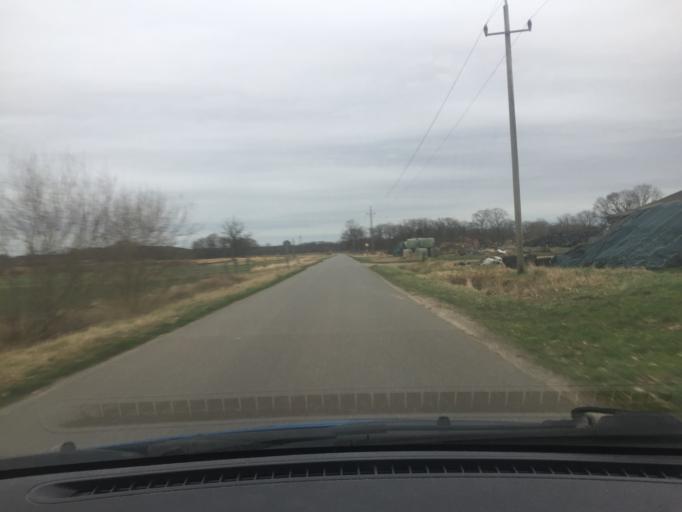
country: DE
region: Lower Saxony
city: Salzhausen
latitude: 53.2236
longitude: 10.1829
